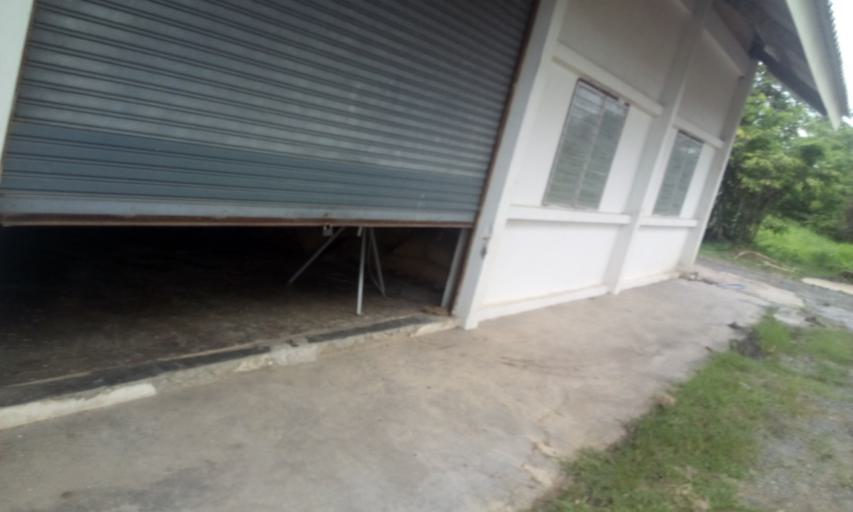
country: TH
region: Pathum Thani
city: Ban Lam Luk Ka
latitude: 13.9907
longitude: 100.8373
